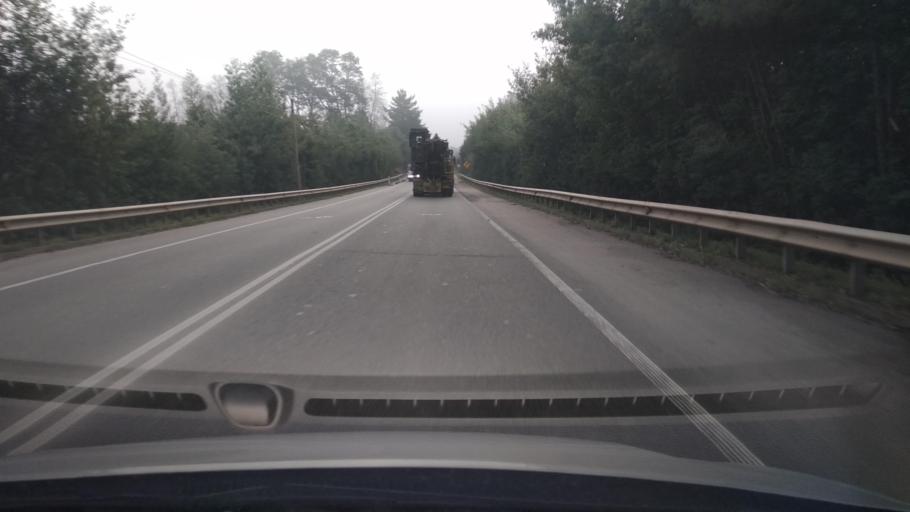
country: CL
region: Los Lagos
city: Las Animas
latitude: -39.7688
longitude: -73.2237
